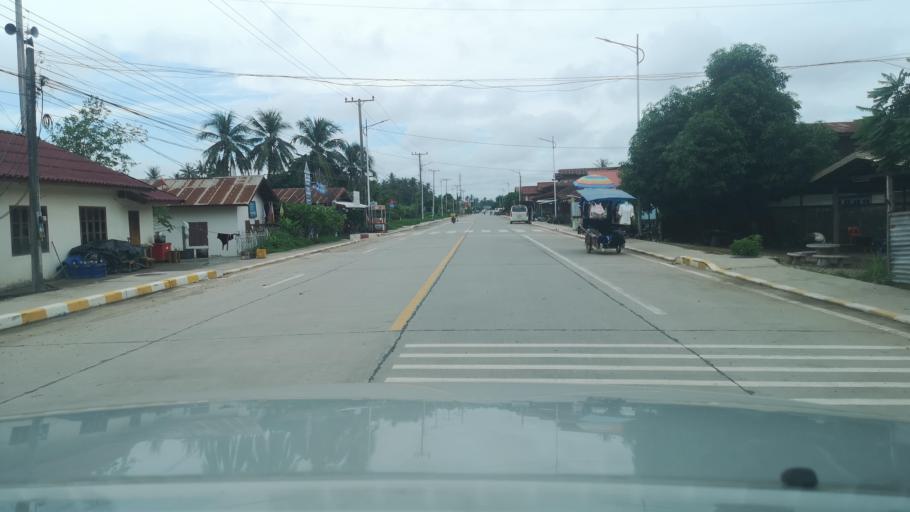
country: TH
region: Nong Khai
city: Tha Bo
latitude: 17.8161
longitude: 102.6651
